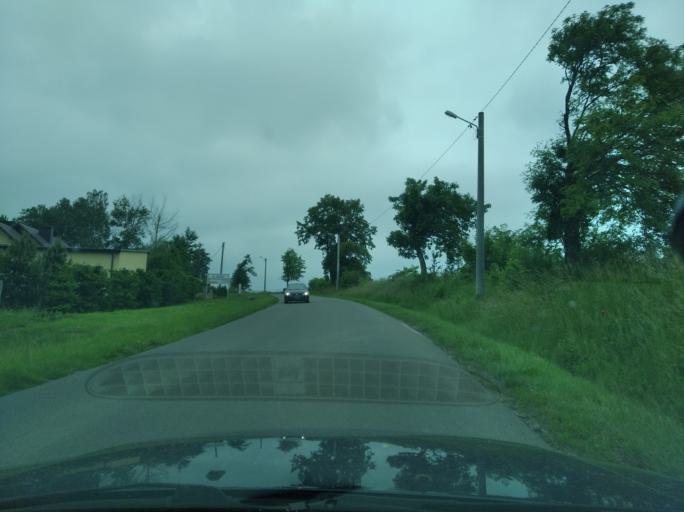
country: PL
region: Subcarpathian Voivodeship
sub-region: Powiat ropczycko-sedziszowski
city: Sedziszow Malopolski
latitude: 50.0477
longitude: 21.6962
